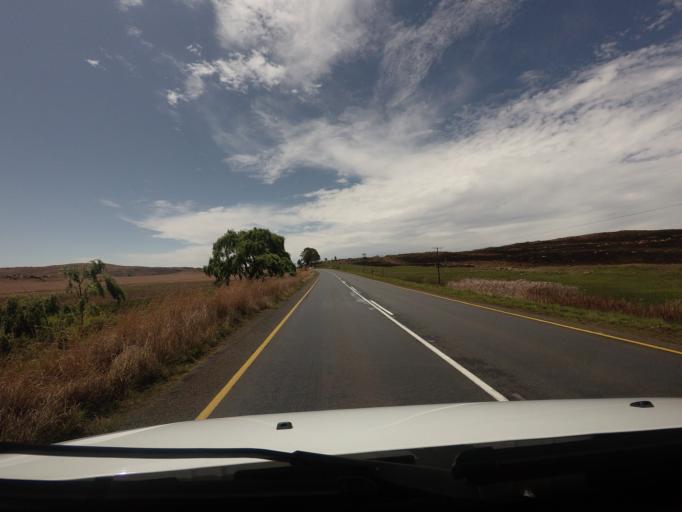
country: ZA
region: Mpumalanga
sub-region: Nkangala District Municipality
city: Belfast
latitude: -25.3922
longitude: 30.1298
